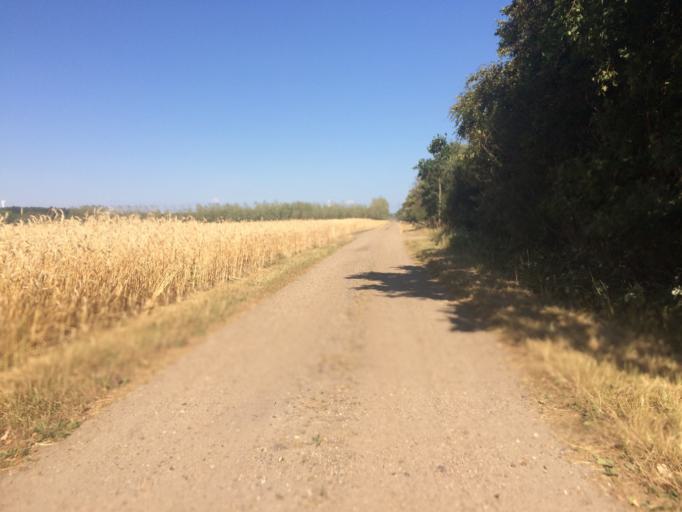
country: DK
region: Central Jutland
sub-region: Holstebro Kommune
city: Vinderup
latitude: 56.5769
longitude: 8.8156
